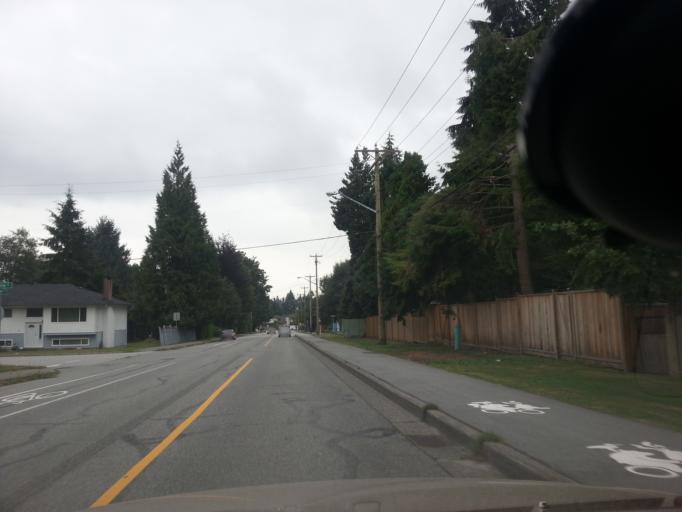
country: CA
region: British Columbia
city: Port Moody
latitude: 49.2729
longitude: -122.8806
